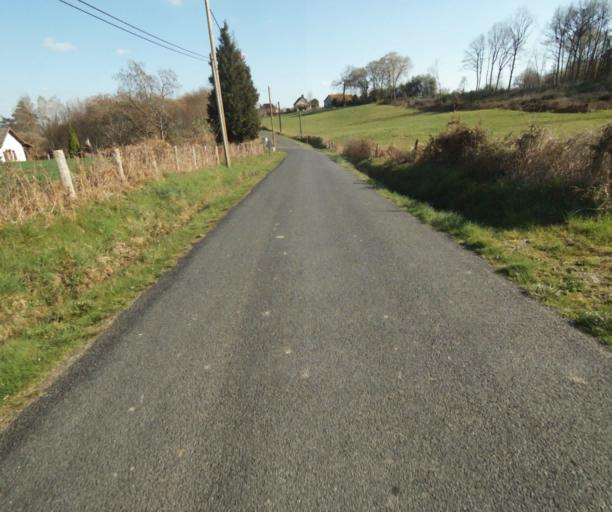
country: FR
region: Limousin
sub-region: Departement de la Correze
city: Saint-Mexant
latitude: 45.3178
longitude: 1.6226
